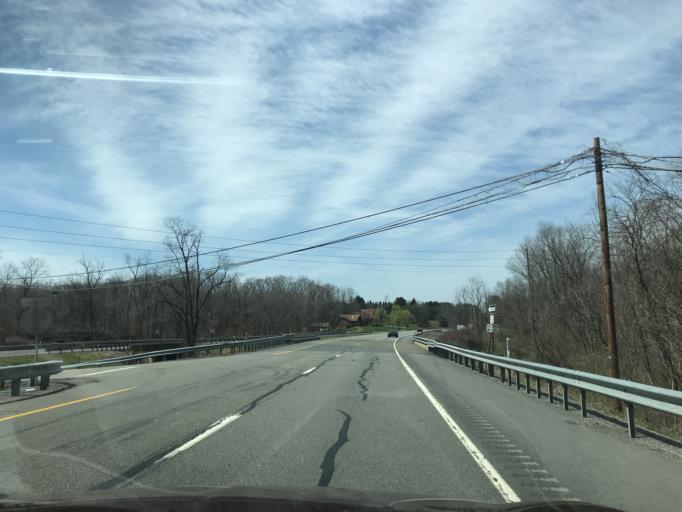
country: US
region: Pennsylvania
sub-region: Union County
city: Lewisburg
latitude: 40.9258
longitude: -76.8645
